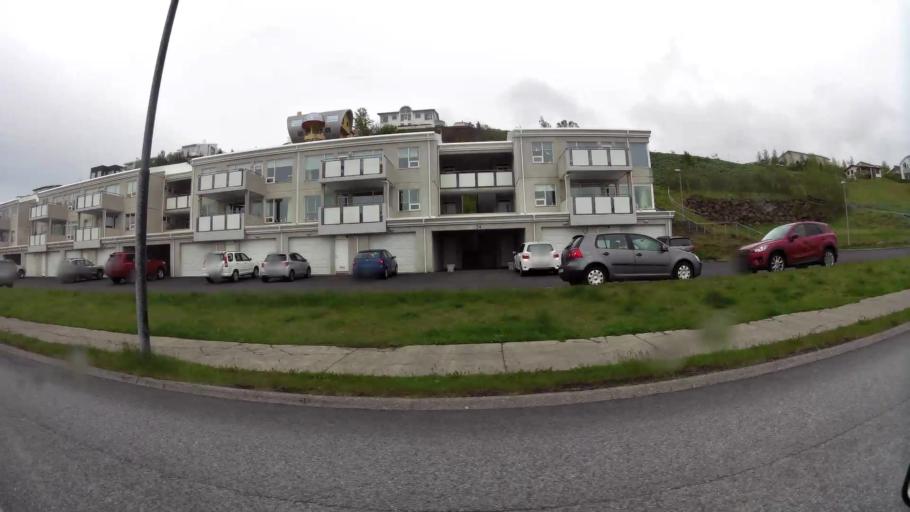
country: IS
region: Capital Region
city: Hafnarfjoerdur
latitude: 64.0632
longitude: -21.9266
